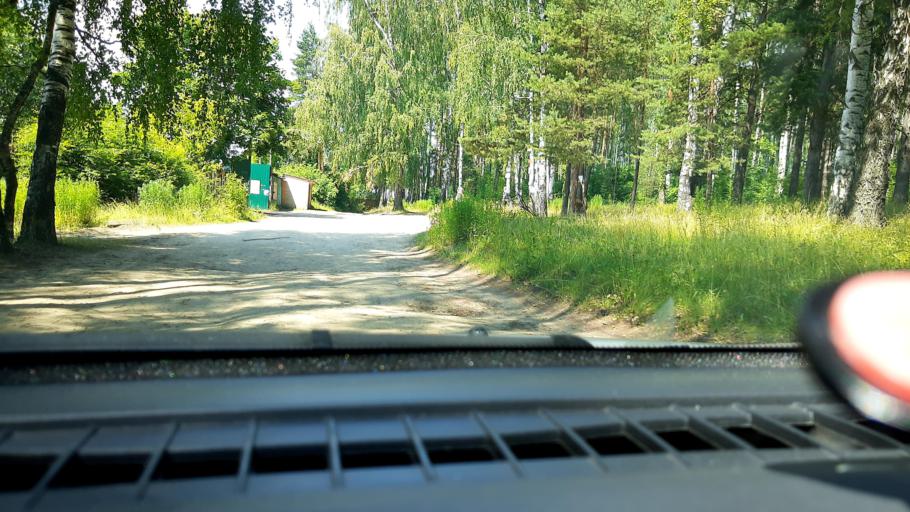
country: RU
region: Nizjnij Novgorod
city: Neklyudovo
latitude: 56.4505
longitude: 43.9964
